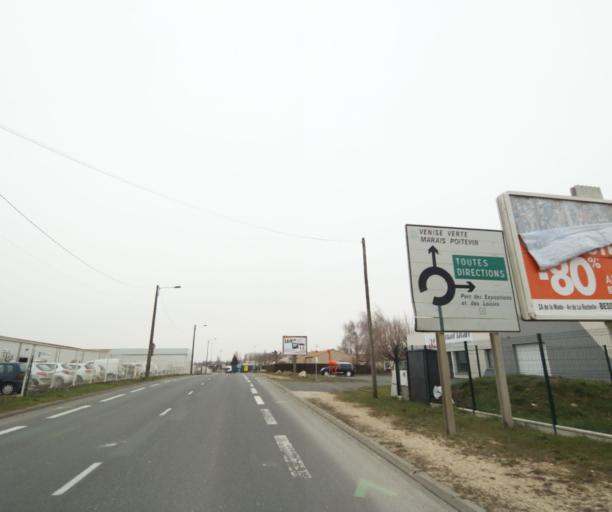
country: FR
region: Poitou-Charentes
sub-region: Departement des Deux-Sevres
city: Bessines
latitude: 46.3127
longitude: -0.4972
